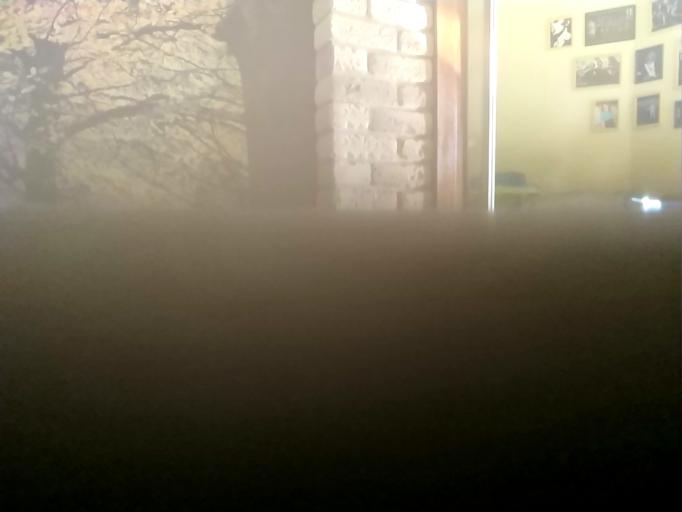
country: RU
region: Smolensk
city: Temkino
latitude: 54.8842
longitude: 34.9816
